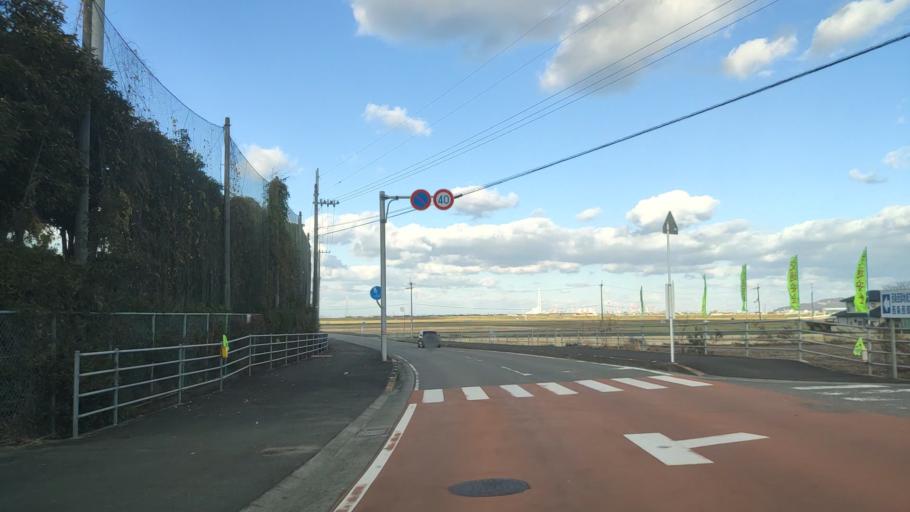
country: JP
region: Ehime
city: Saijo
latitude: 33.8986
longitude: 133.1346
